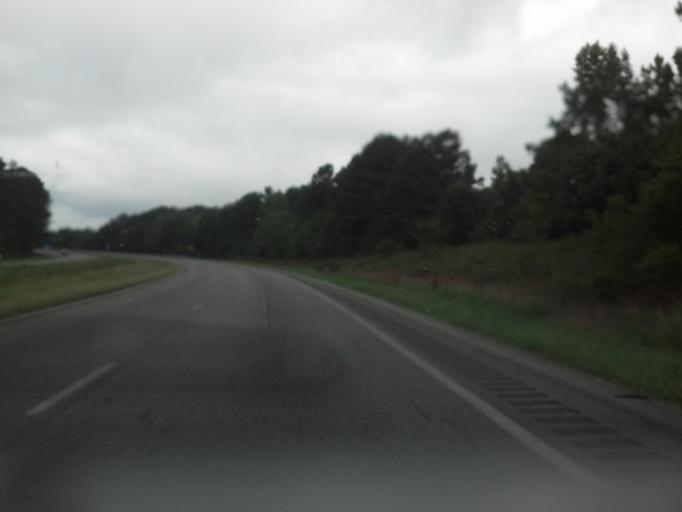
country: US
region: North Carolina
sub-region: Nash County
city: Rocky Mount
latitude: 35.9577
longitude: -77.7671
